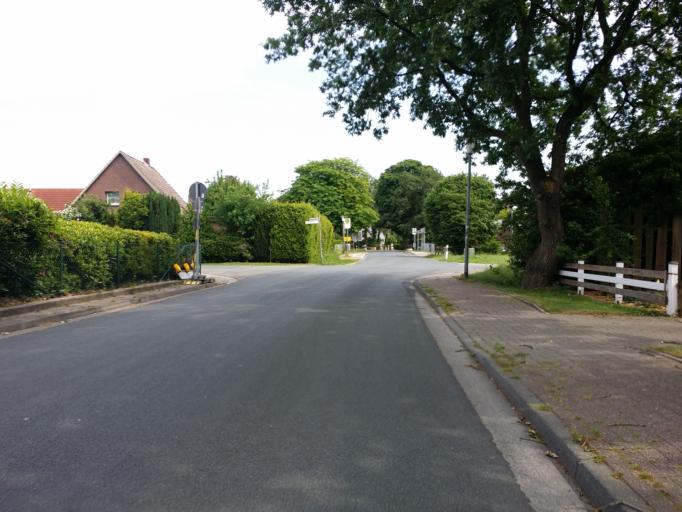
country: DE
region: Lower Saxony
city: Rastede
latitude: 53.1990
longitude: 8.2035
